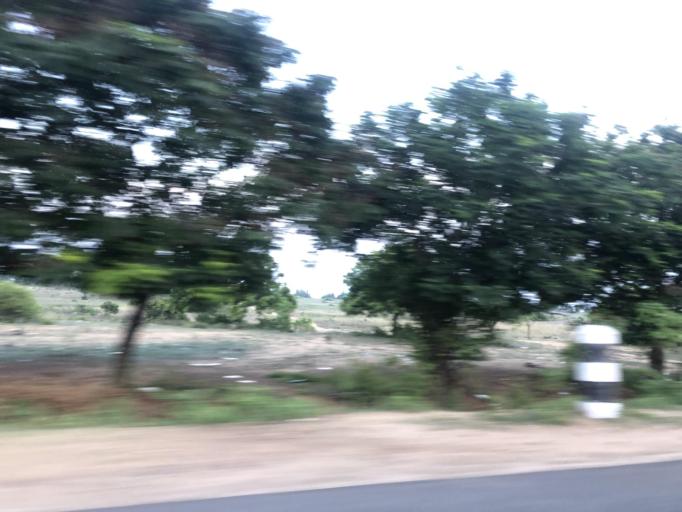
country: IN
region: Tamil Nadu
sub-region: Kancheepuram
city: Mamallapuram
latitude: 12.7557
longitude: 80.2428
